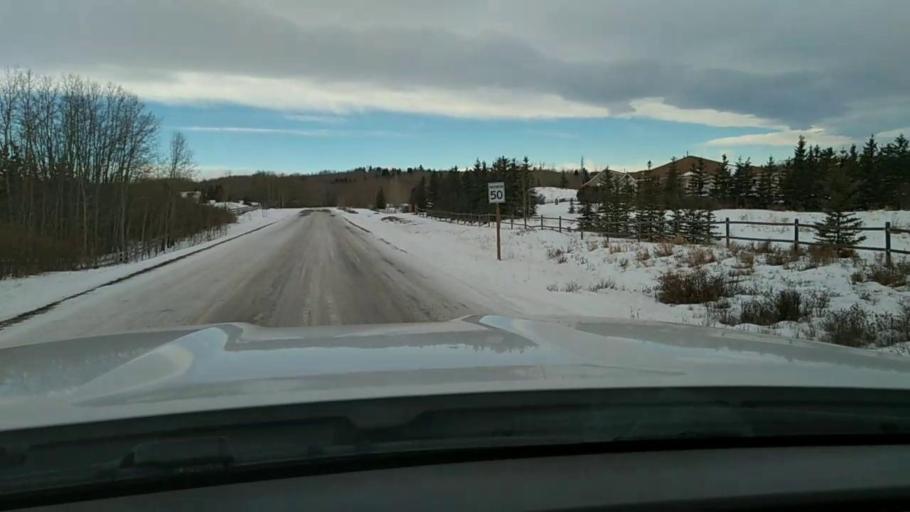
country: CA
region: Alberta
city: Cochrane
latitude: 51.1988
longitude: -114.2814
